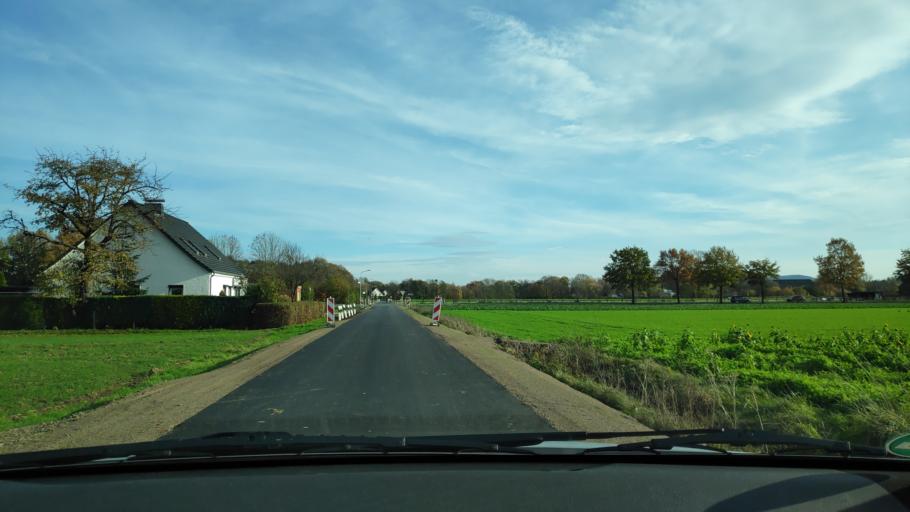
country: DE
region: North Rhine-Westphalia
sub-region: Regierungsbezirk Detmold
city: Minden
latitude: 52.2830
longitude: 8.8629
